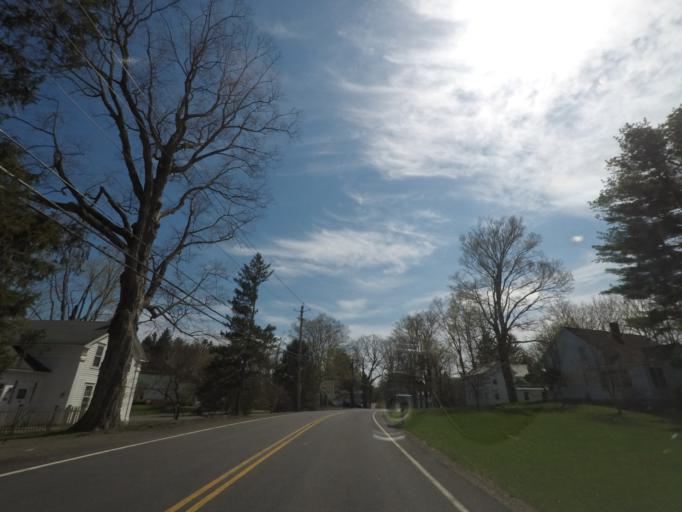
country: US
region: New York
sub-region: Columbia County
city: Chatham
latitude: 42.3963
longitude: -73.5262
